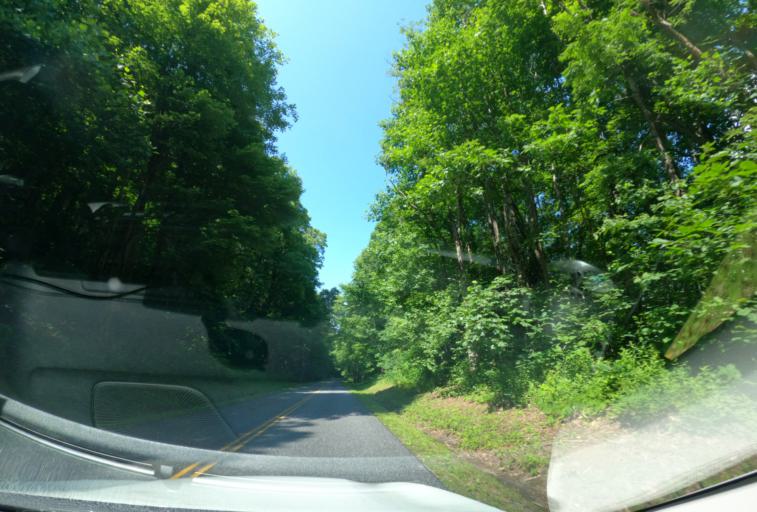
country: US
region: North Carolina
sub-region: Haywood County
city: Hazelwood
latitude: 35.4348
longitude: -83.0716
